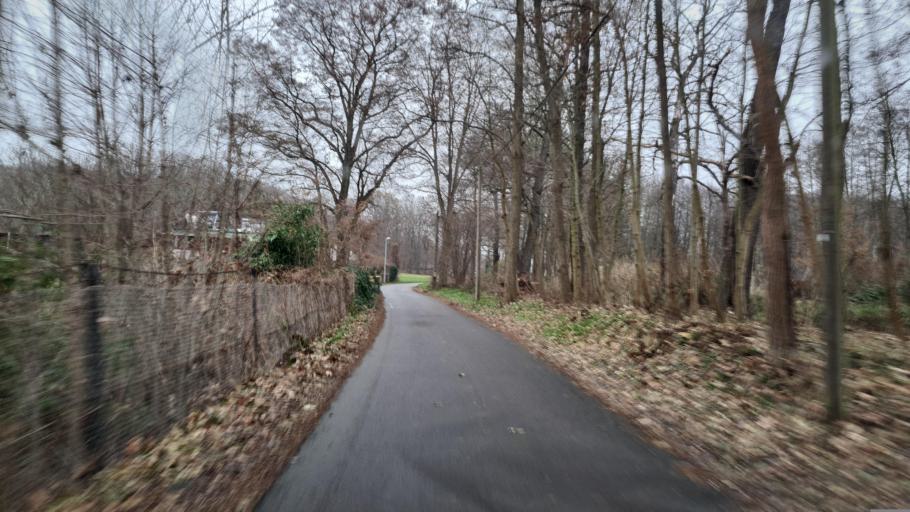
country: DE
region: Brandenburg
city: Kolkwitz
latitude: 51.7477
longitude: 14.2657
